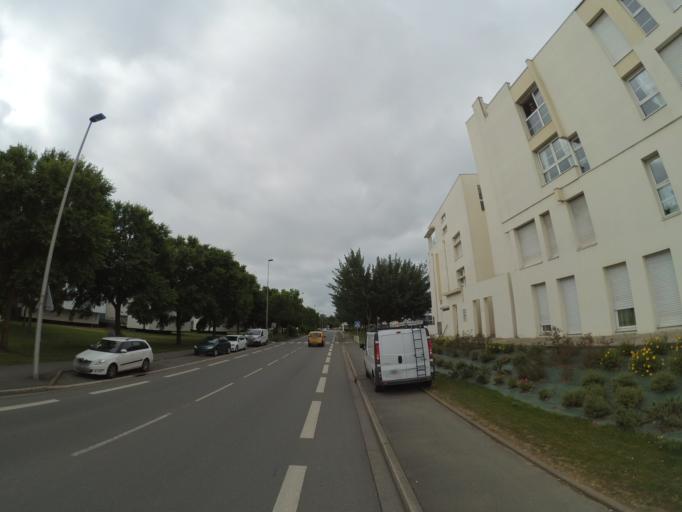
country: FR
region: Poitou-Charentes
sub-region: Departement de la Charente-Maritime
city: La Rochelle
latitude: 46.1456
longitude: -1.1526
